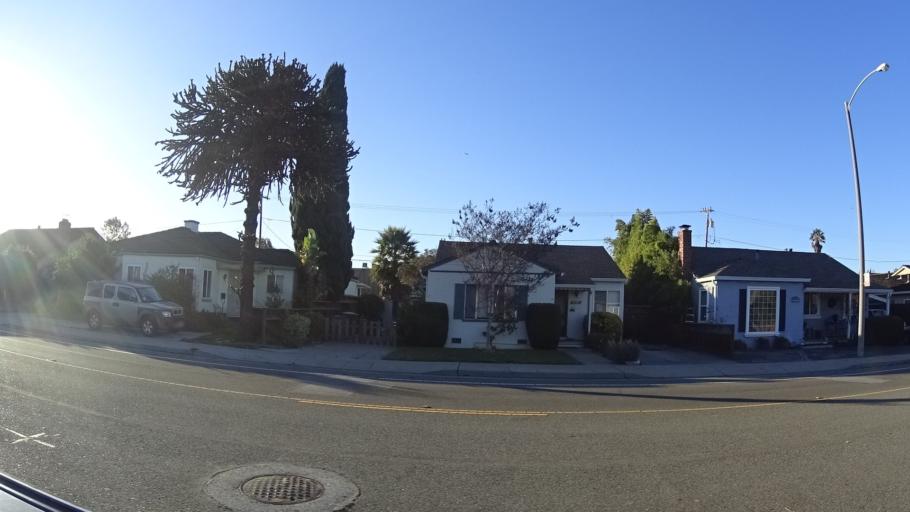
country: US
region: California
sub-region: Santa Clara County
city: Sunnyvale
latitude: 37.3695
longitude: -122.0314
